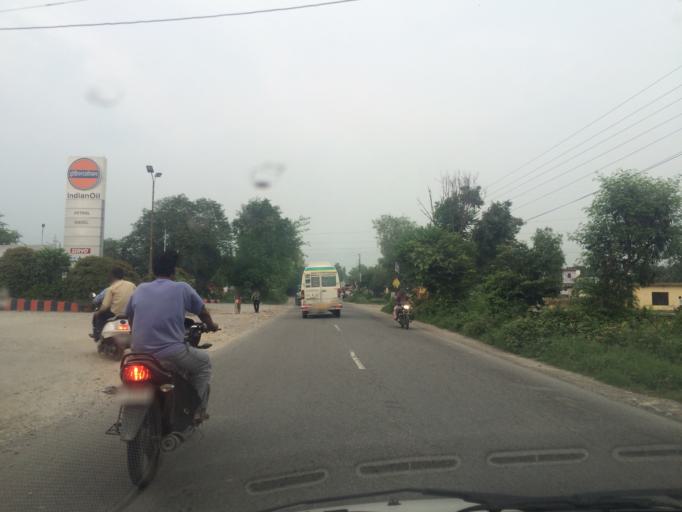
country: IN
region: Uttarakhand
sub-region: Dehradun
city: Doiwala
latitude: 30.1803
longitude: 78.1364
